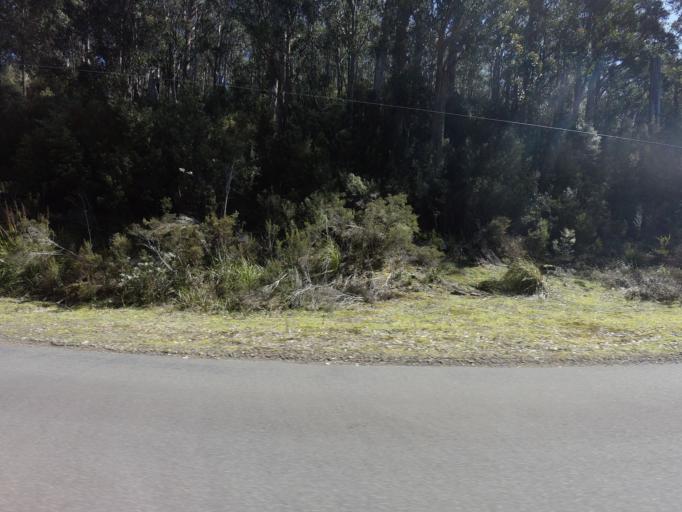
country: AU
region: Tasmania
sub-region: Derwent Valley
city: New Norfolk
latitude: -42.7379
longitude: 146.4956
